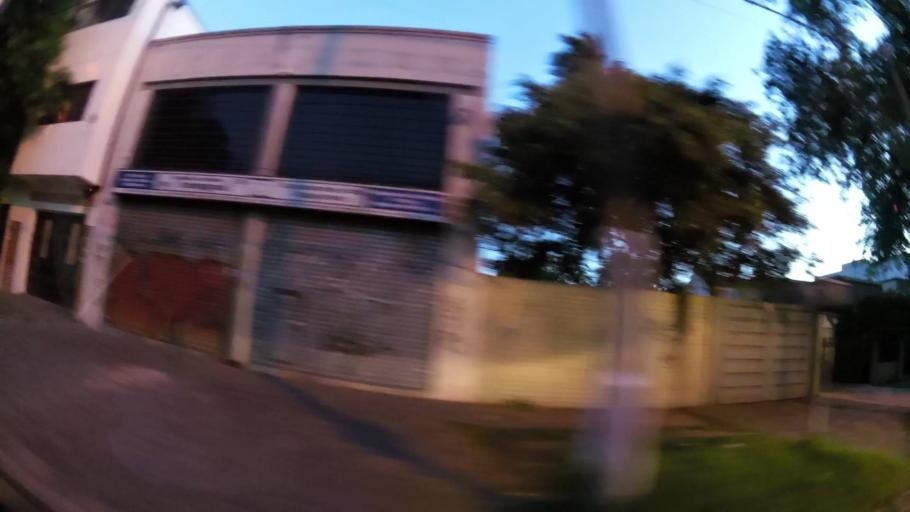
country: AR
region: Buenos Aires
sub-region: Partido de Quilmes
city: Quilmes
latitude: -34.7710
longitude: -58.2090
